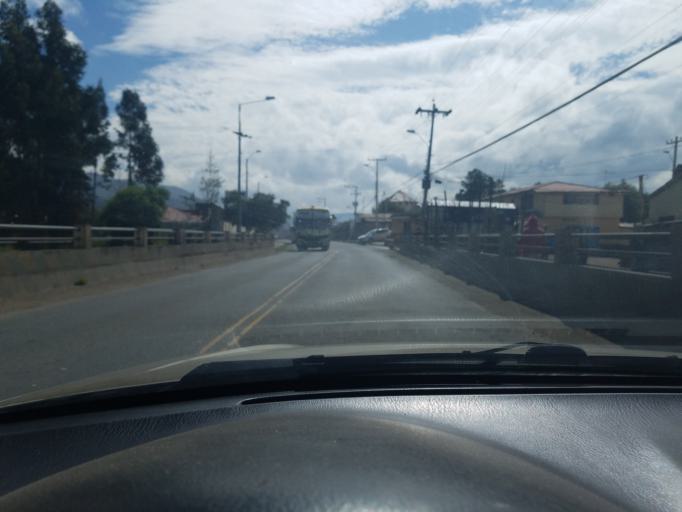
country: EC
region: Azuay
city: Llacao
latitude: -2.8619
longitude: -78.9358
